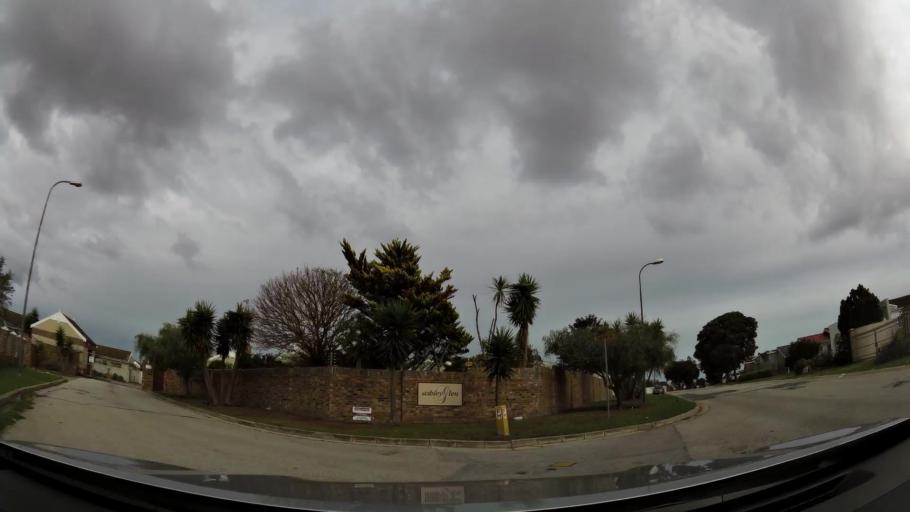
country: ZA
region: Eastern Cape
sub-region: Nelson Mandela Bay Metropolitan Municipality
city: Port Elizabeth
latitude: -33.9357
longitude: 25.5063
